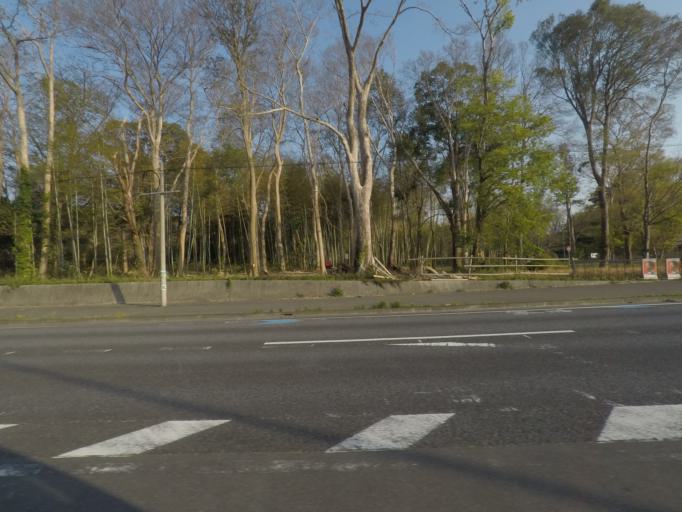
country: JP
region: Chiba
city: Yotsukaido
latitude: 35.6392
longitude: 140.1740
